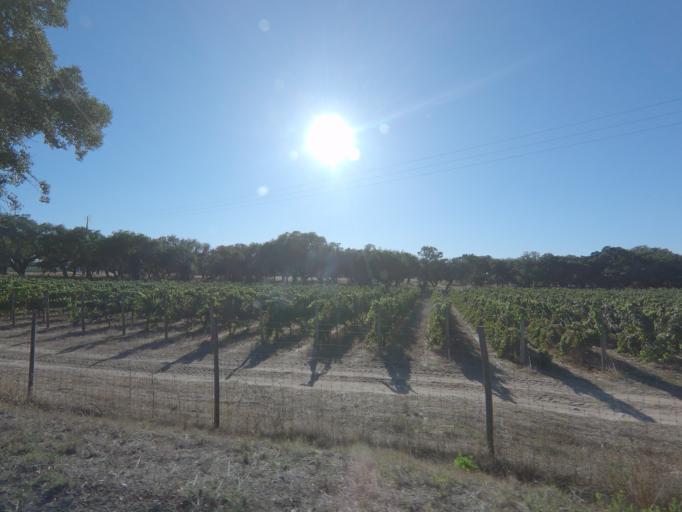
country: PT
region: Setubal
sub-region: Palmela
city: Quinta do Anjo
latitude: 38.5419
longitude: -8.9854
